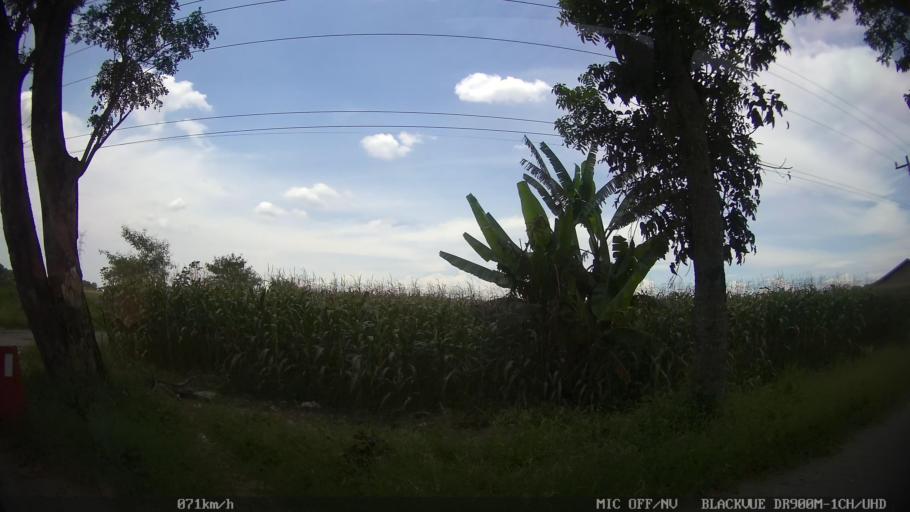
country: ID
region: North Sumatra
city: Binjai
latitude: 3.5912
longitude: 98.5106
